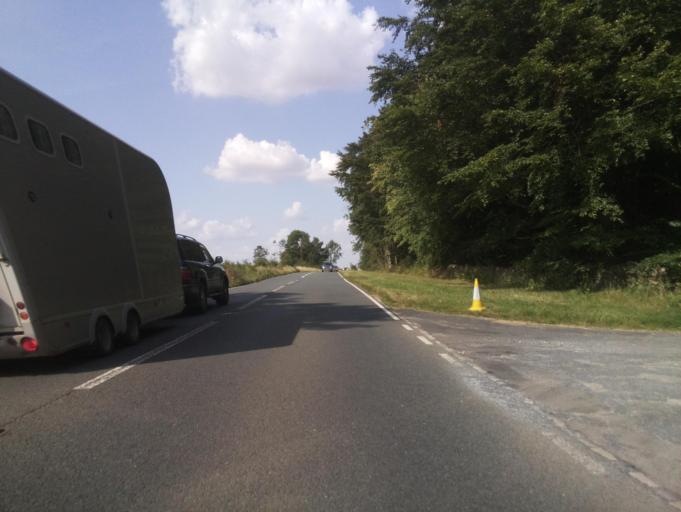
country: GB
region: England
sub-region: Gloucestershire
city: Cirencester
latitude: 51.7608
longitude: -1.9341
